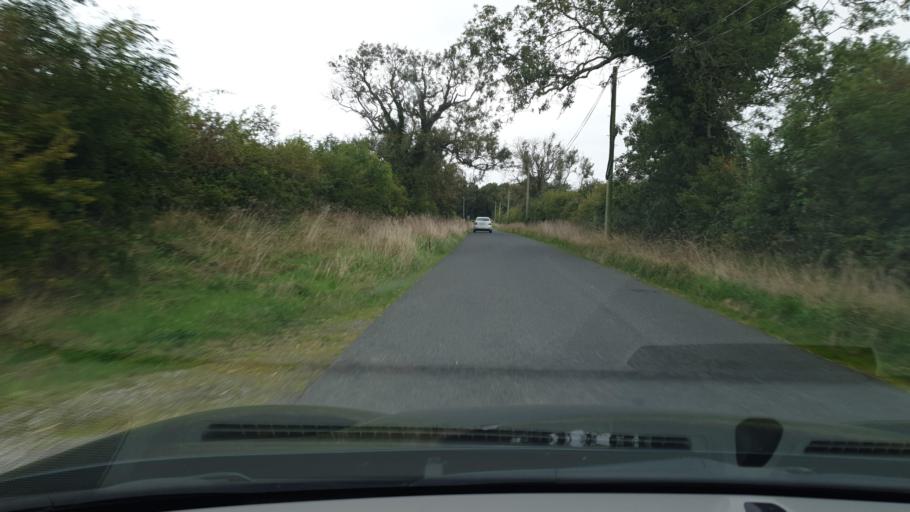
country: IE
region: Leinster
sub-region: An Mhi
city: Dunshaughlin
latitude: 53.5460
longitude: -6.5368
